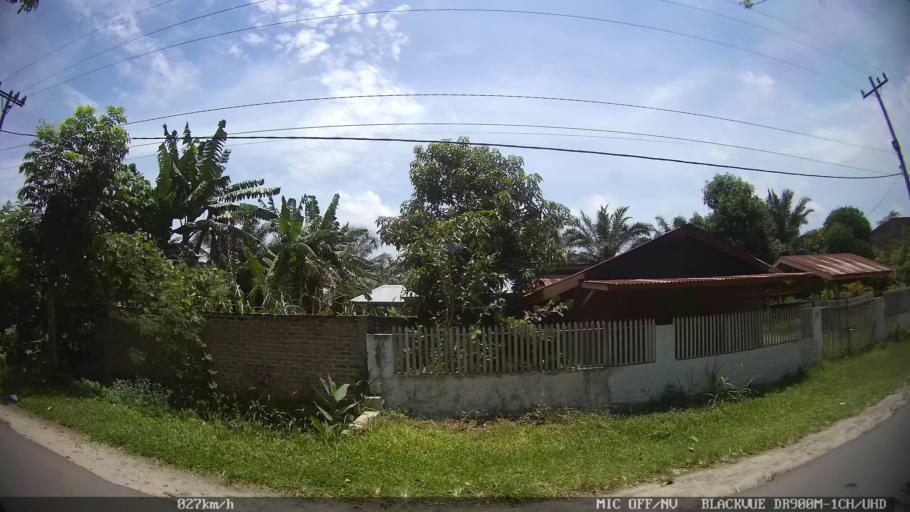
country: ID
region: North Sumatra
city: Percut
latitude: 3.5414
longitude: 98.8747
